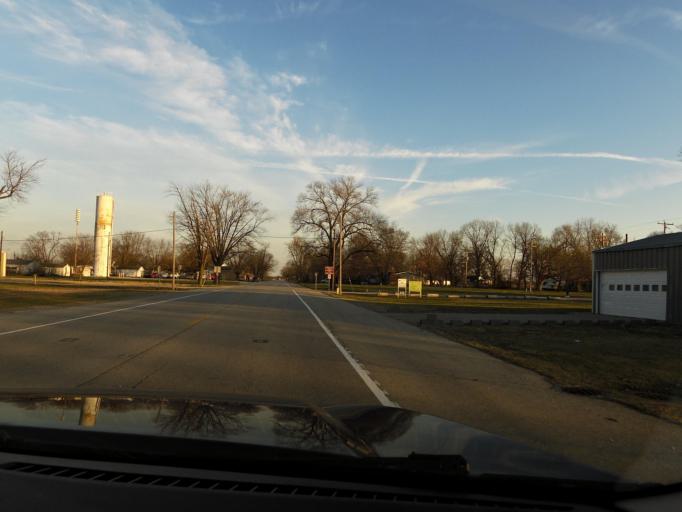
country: US
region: Illinois
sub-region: Fayette County
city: Vandalia
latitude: 38.8007
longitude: -89.0864
